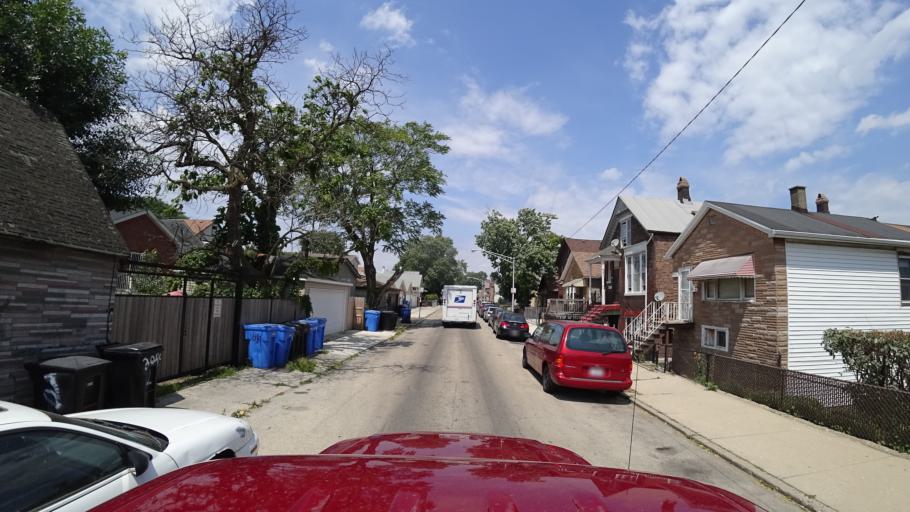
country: US
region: Illinois
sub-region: Cook County
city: Chicago
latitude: 41.8385
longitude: -87.6511
